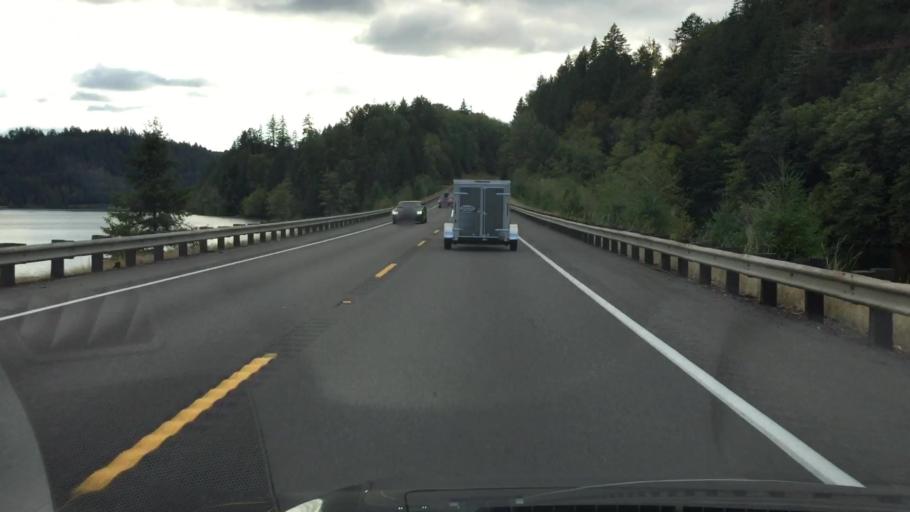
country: US
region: Washington
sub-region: Lewis County
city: Morton
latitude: 46.5152
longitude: -122.5692
